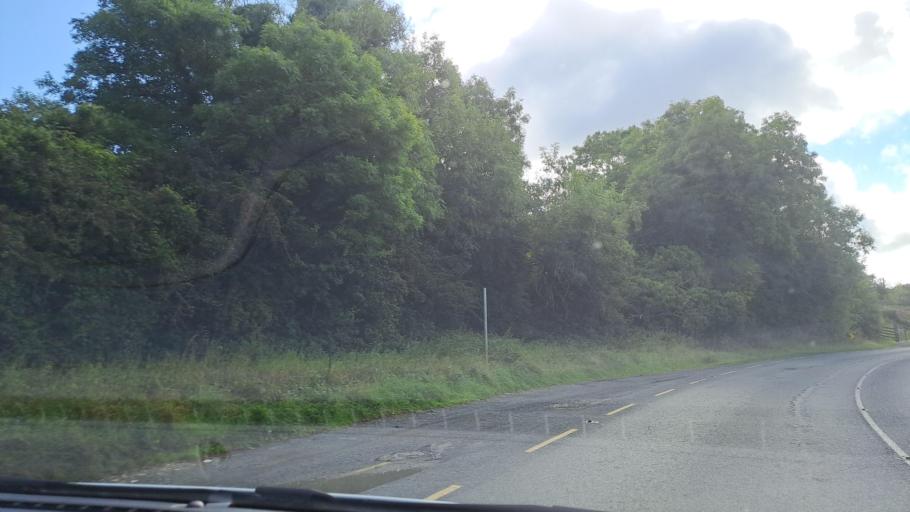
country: IE
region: Ulster
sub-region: An Cabhan
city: Kingscourt
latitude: 53.9354
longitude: -6.7786
